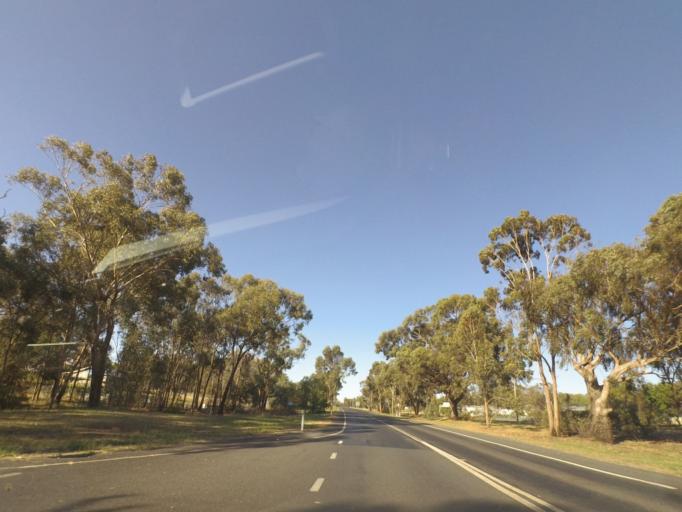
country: AU
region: New South Wales
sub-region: Wagga Wagga
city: Forest Hill
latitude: -35.2735
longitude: 147.7419
